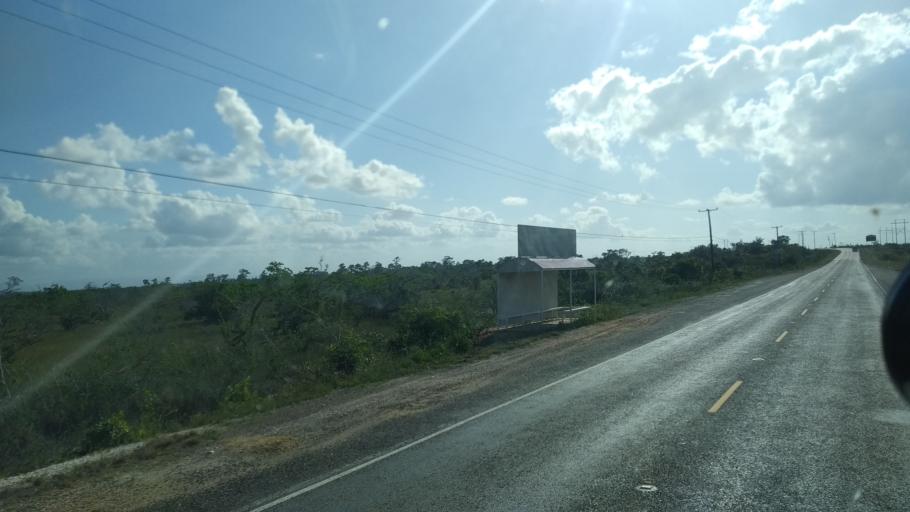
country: BZ
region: Cayo
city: Belmopan
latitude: 17.4050
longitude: -88.4971
